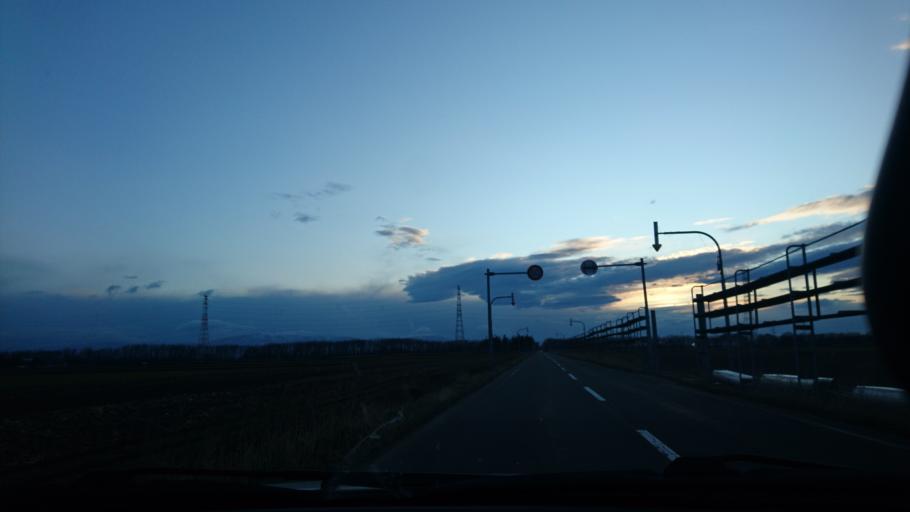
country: JP
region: Hokkaido
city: Tobetsu
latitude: 43.1920
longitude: 141.4321
